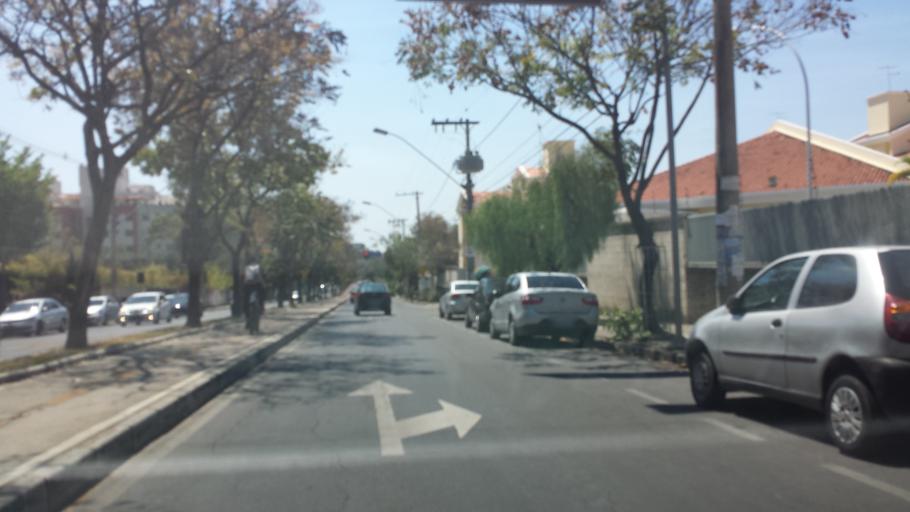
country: BR
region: Minas Gerais
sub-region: Belo Horizonte
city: Belo Horizonte
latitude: -19.8710
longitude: -43.9866
